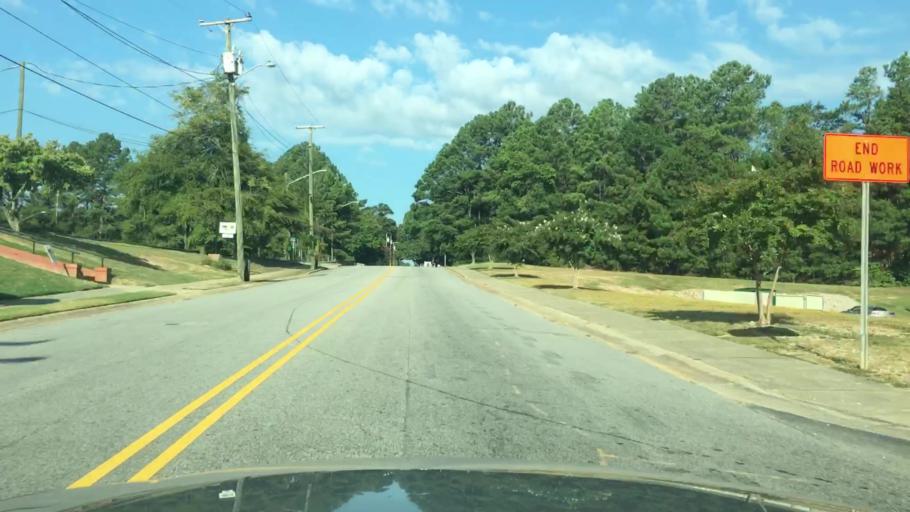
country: US
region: North Carolina
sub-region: Cumberland County
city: Fayetteville
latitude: 35.0609
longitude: -78.8899
